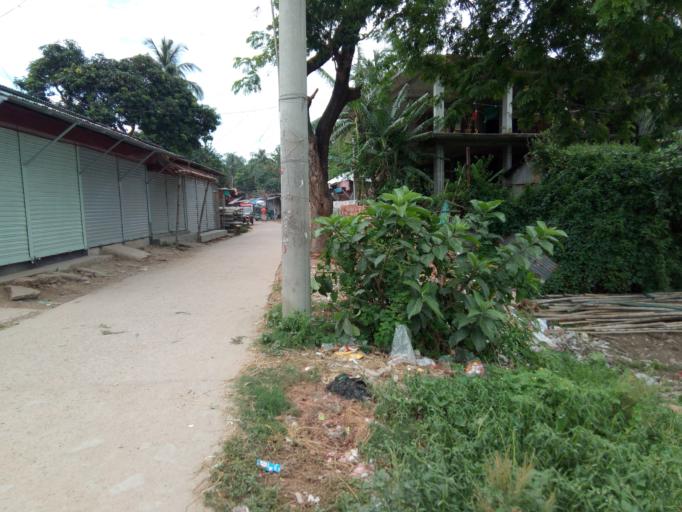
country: BD
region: Dhaka
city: Paltan
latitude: 23.7510
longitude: 90.4850
